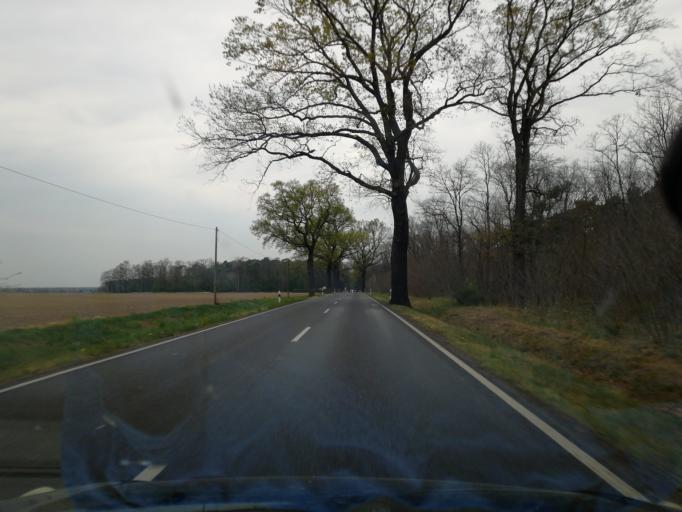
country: DE
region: Brandenburg
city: Calau
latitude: 51.7675
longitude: 13.9032
